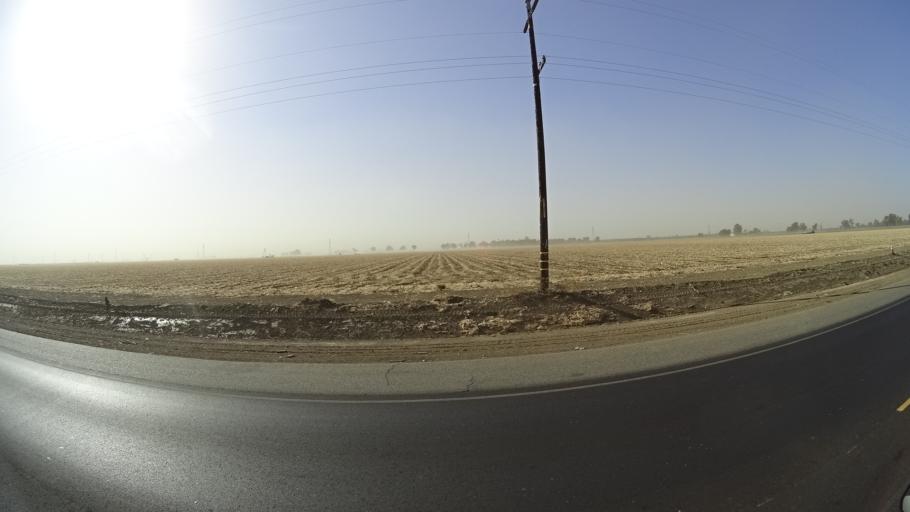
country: US
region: California
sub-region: Yolo County
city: Woodland
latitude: 38.7818
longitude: -121.7285
